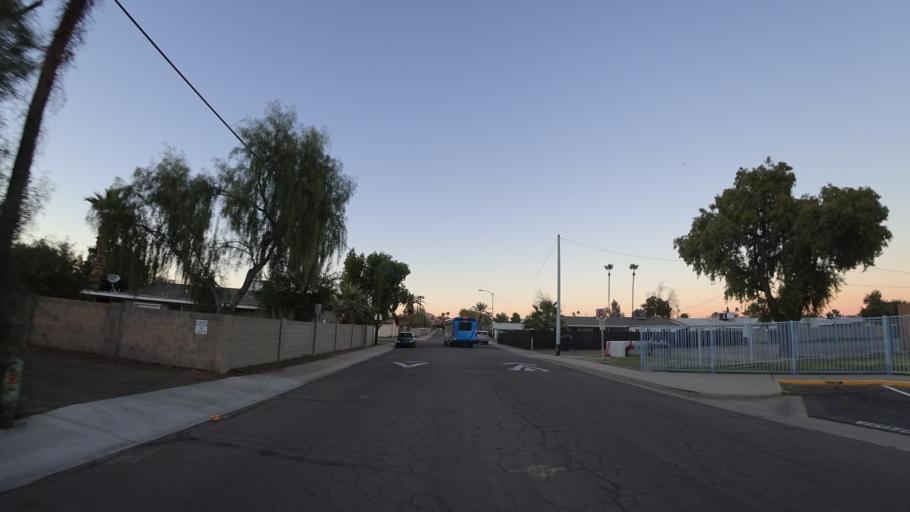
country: US
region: Arizona
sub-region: Maricopa County
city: Tempe Junction
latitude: 33.4184
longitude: -111.9565
